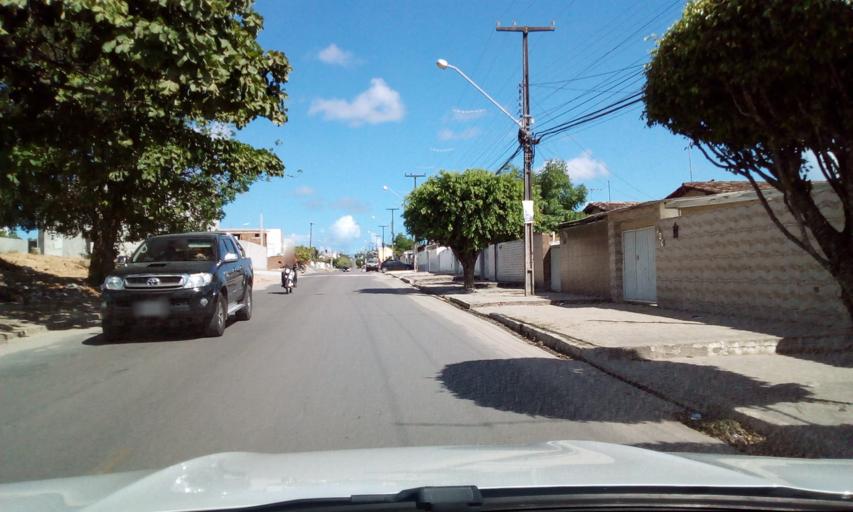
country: BR
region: Paraiba
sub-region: Joao Pessoa
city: Joao Pessoa
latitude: -7.1757
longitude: -34.8875
